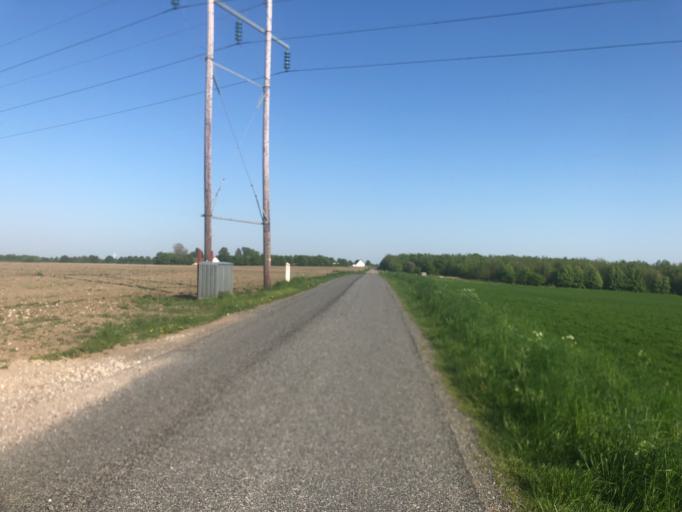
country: DK
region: Zealand
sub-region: Ringsted Kommune
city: Ringsted
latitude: 55.4752
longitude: 11.8159
